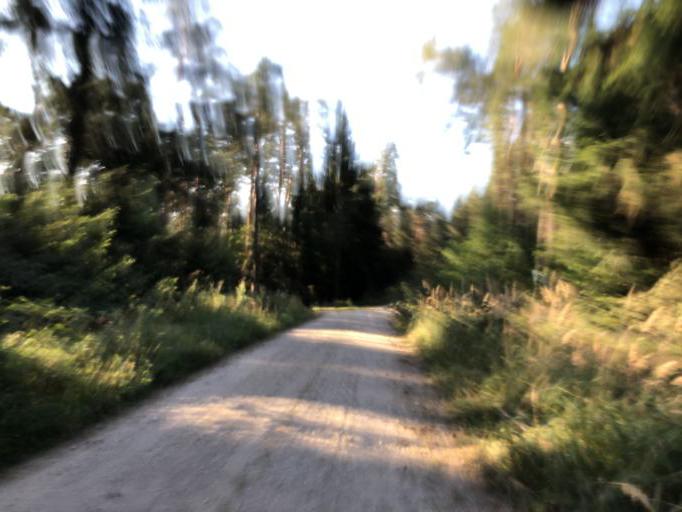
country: DE
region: Bavaria
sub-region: Regierungsbezirk Mittelfranken
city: Uttenreuth
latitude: 49.5630
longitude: 11.0850
